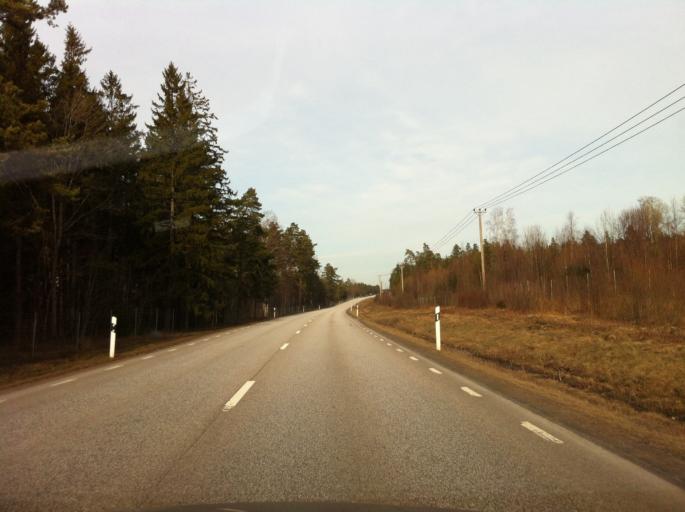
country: SE
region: Vaestra Goetaland
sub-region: Gullspangs Kommun
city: Gullspang
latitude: 58.9340
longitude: 14.0365
